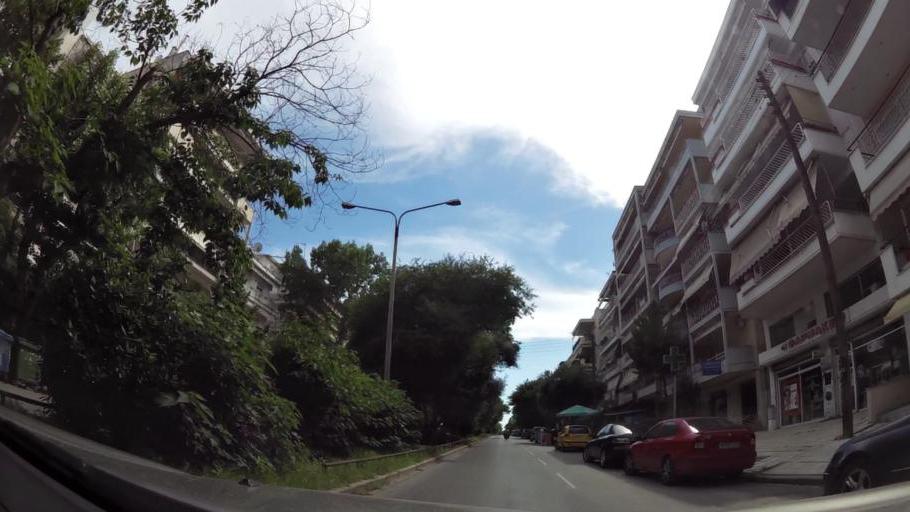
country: GR
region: Central Macedonia
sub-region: Nomos Thessalonikis
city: Kalamaria
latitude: 40.5869
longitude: 22.9488
